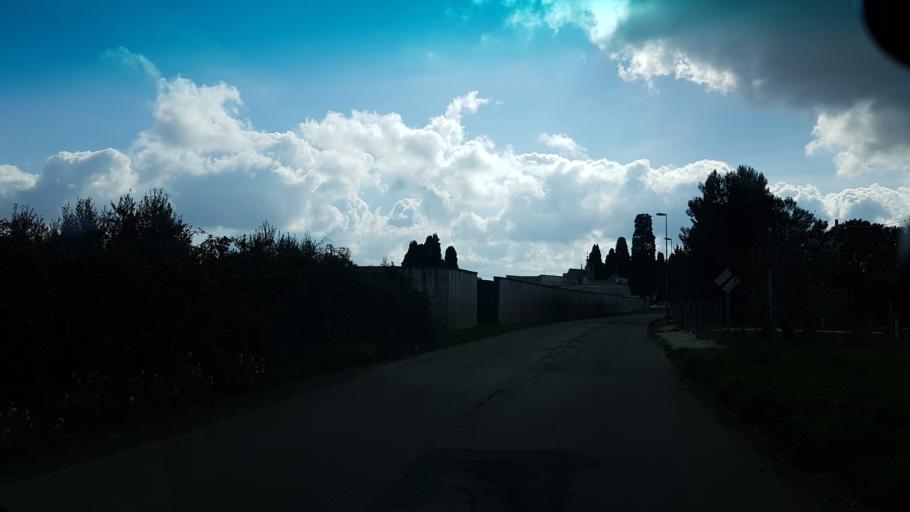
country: IT
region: Apulia
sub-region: Provincia di Lecce
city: Squinzano
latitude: 40.4437
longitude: 18.0443
